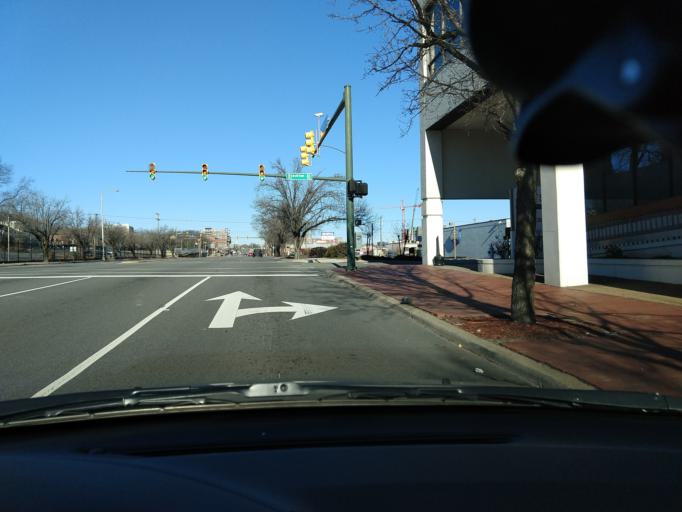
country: US
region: Virginia
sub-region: City of Richmond
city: Richmond
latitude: 37.5211
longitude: -77.4390
